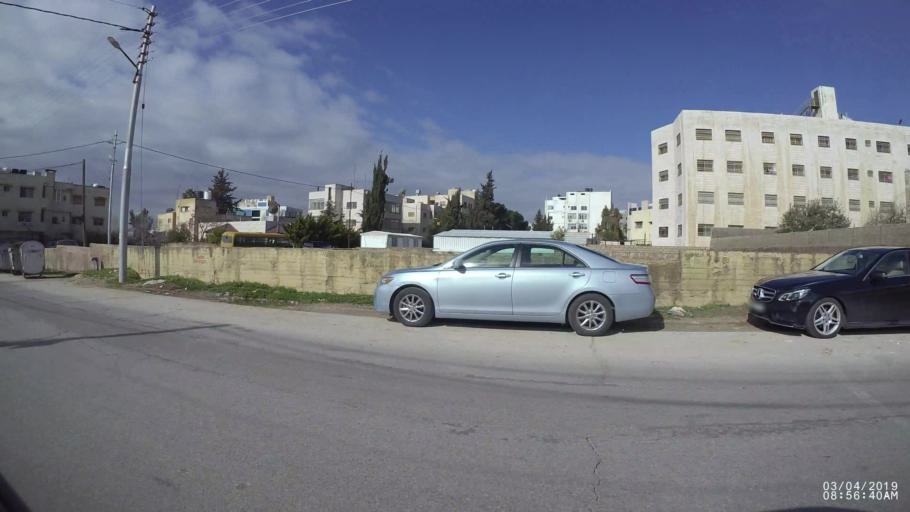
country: JO
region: Amman
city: Wadi as Sir
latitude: 31.9541
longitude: 35.8428
